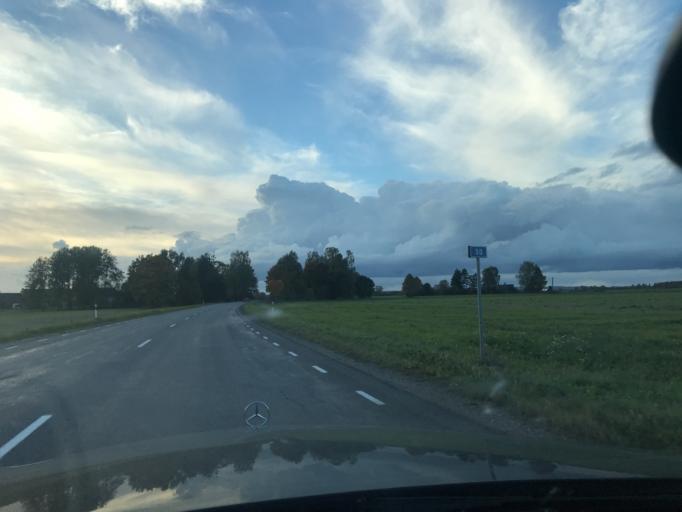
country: EE
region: Vorumaa
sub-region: Antsla vald
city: Vana-Antsla
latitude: 57.8956
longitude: 26.4895
